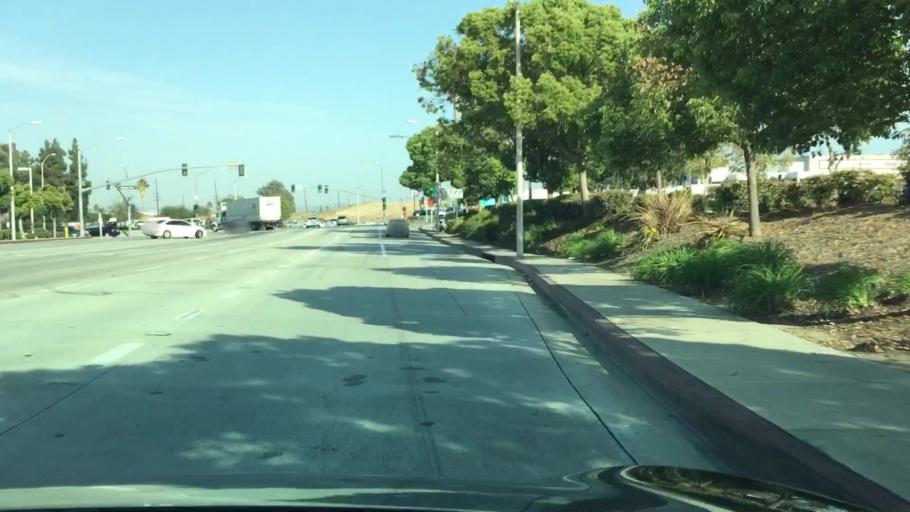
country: US
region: California
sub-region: Los Angeles County
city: La Puente
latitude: 34.0002
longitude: -117.9321
